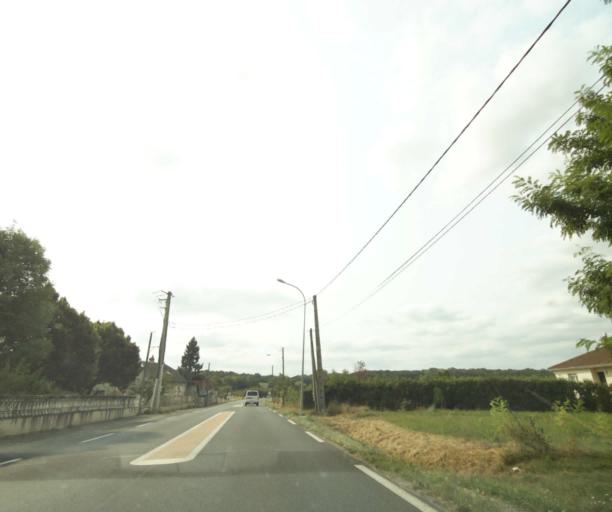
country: FR
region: Centre
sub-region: Departement de l'Indre
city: Clion
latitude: 46.9436
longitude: 1.2200
